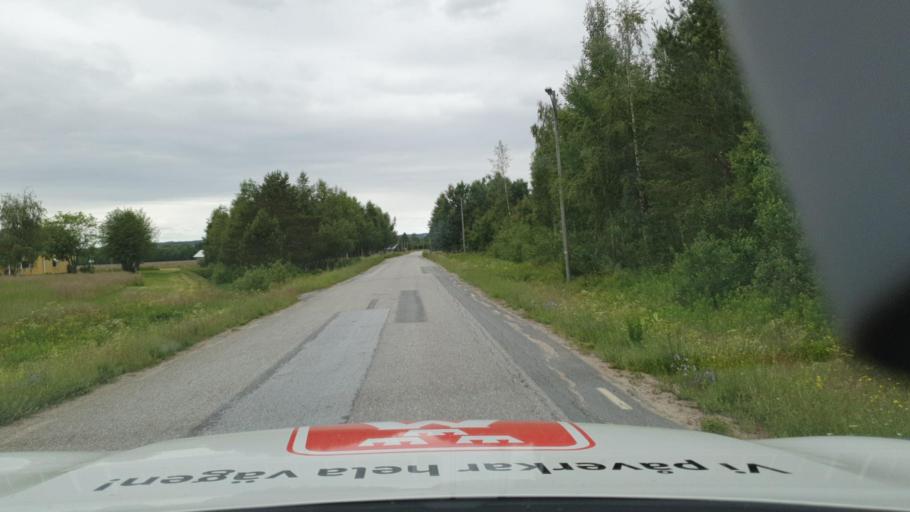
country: SE
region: Vaesterbotten
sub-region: Nordmalings Kommun
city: Nordmaling
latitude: 63.5377
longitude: 19.3976
